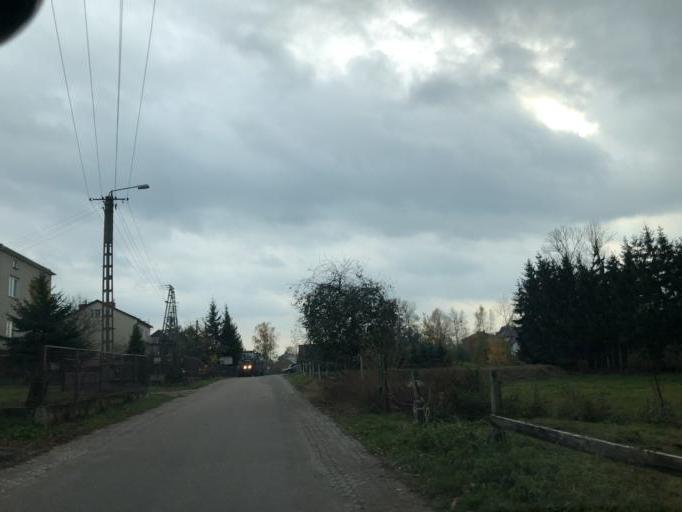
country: PL
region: Podlasie
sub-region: Lomza
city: Lomza
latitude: 53.1582
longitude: 22.0029
